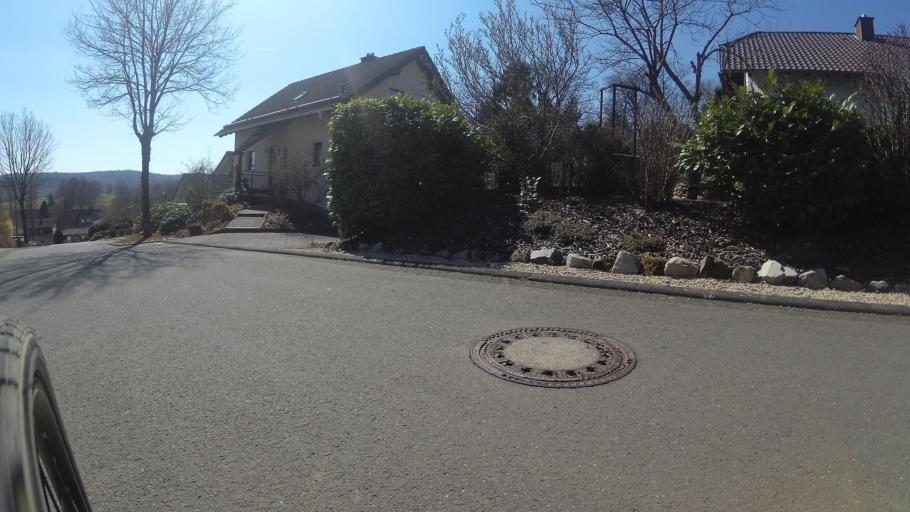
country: DE
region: Rheinland-Pfalz
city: Abentheuer
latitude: 49.6377
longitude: 7.1026
